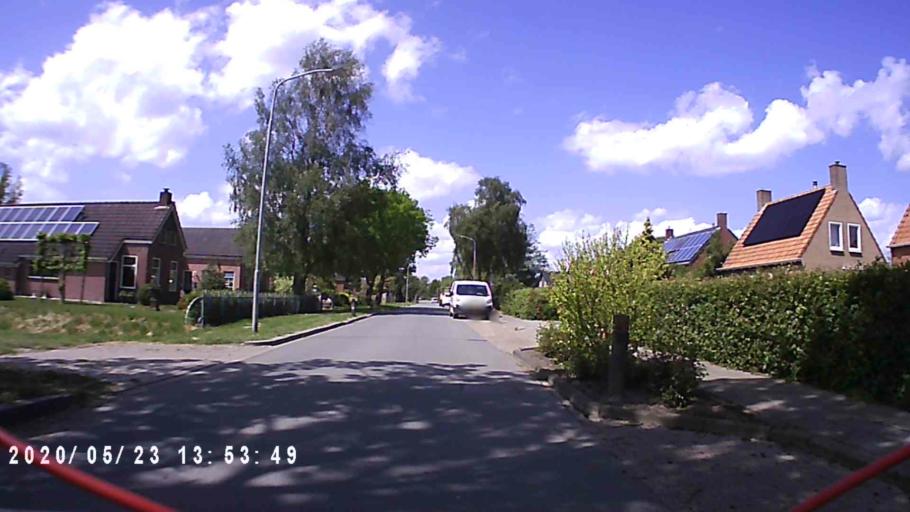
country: NL
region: Groningen
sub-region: Gemeente  Oldambt
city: Winschoten
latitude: 53.2706
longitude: 7.0340
